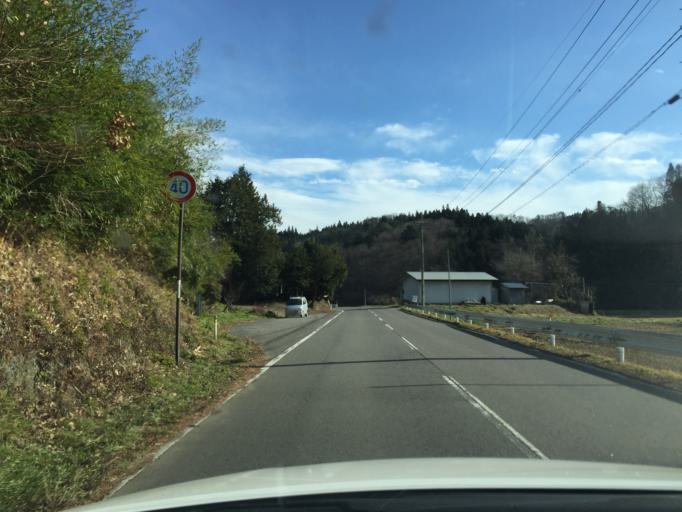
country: JP
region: Fukushima
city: Funehikimachi-funehiki
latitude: 37.2776
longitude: 140.6084
